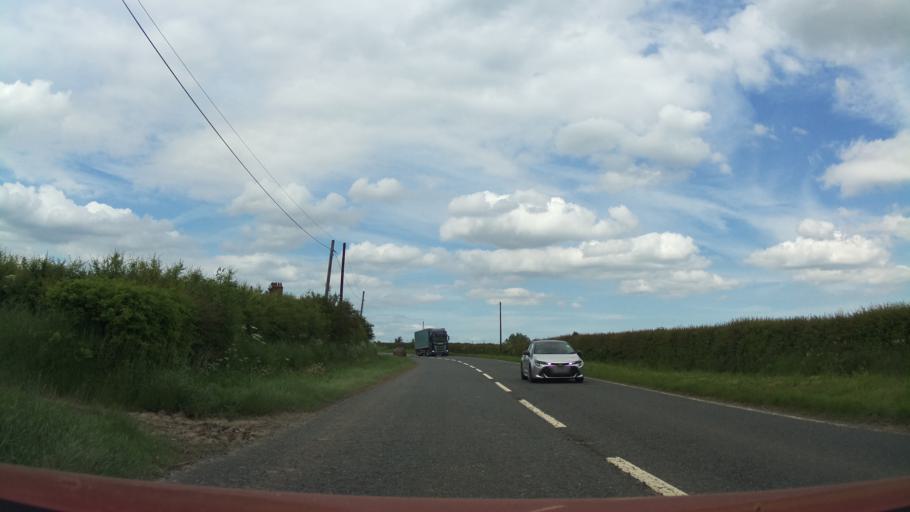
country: GB
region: England
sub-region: Herefordshire
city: Ledbury
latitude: 52.0128
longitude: -2.4800
